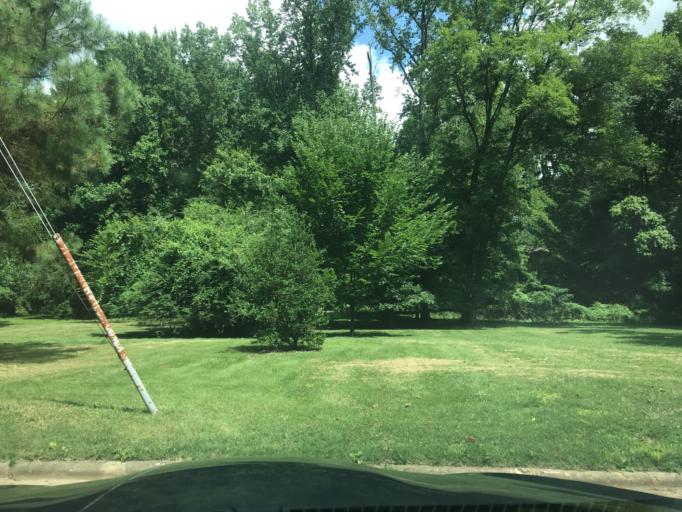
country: US
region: North Carolina
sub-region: Wake County
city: West Raleigh
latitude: 35.8352
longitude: -78.6254
